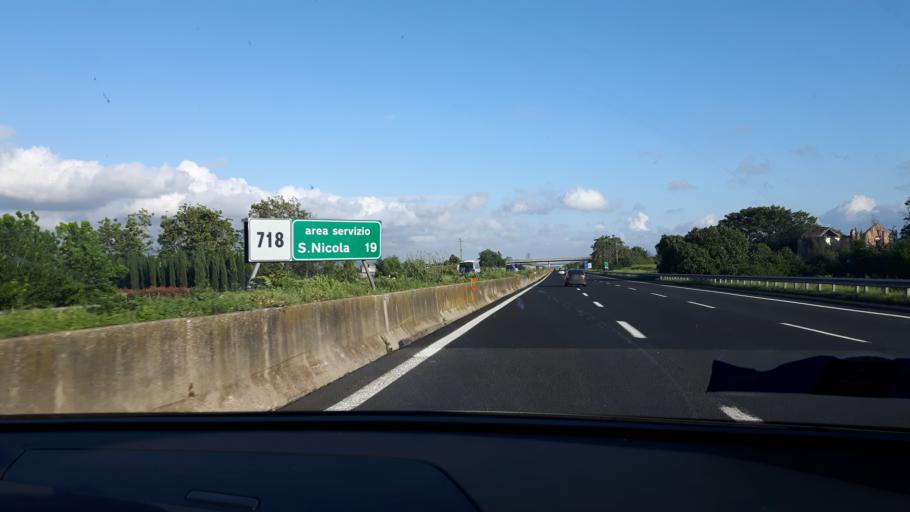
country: IT
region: Campania
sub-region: Provincia di Caserta
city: Pignataro Maggiore
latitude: 41.1769
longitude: 14.1664
